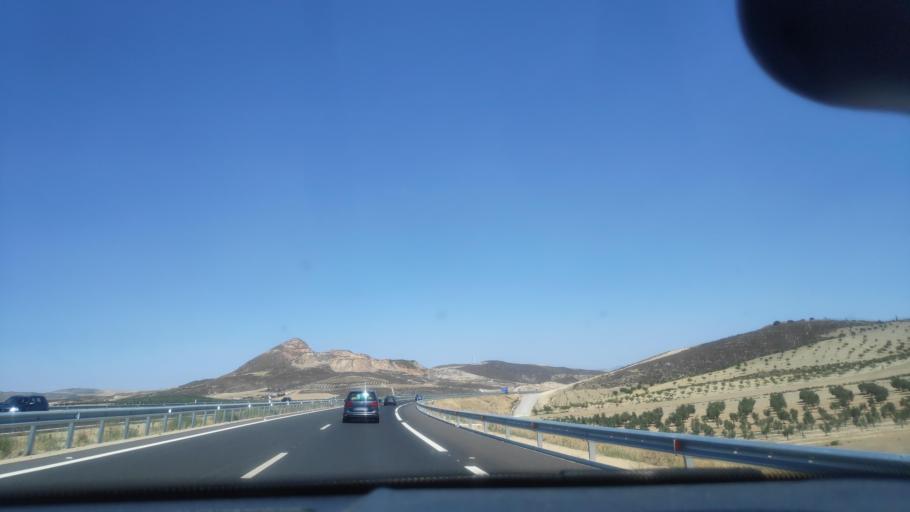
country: ES
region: Andalusia
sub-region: Provincia de Granada
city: Alhendin
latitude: 37.0898
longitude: -3.6700
